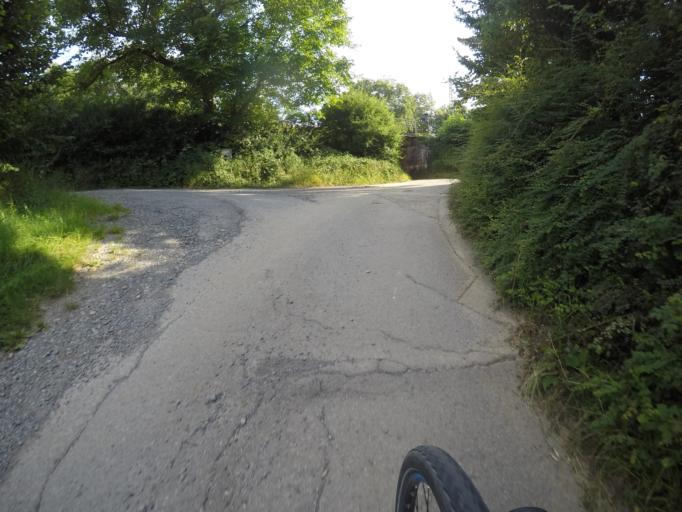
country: DE
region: Baden-Wuerttemberg
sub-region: Regierungsbezirk Stuttgart
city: Rutesheim
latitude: 48.7931
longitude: 8.9767
